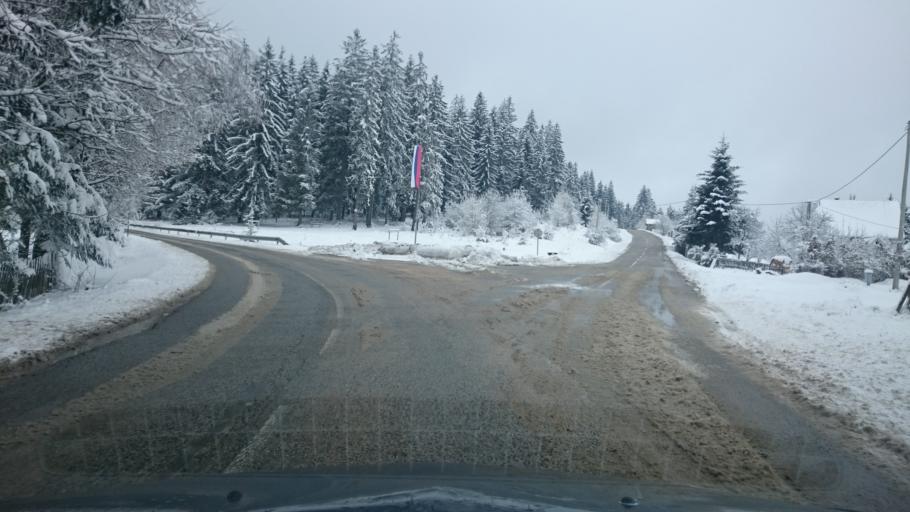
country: BA
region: Republika Srpska
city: Skender Vakuf
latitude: 44.5032
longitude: 17.3600
